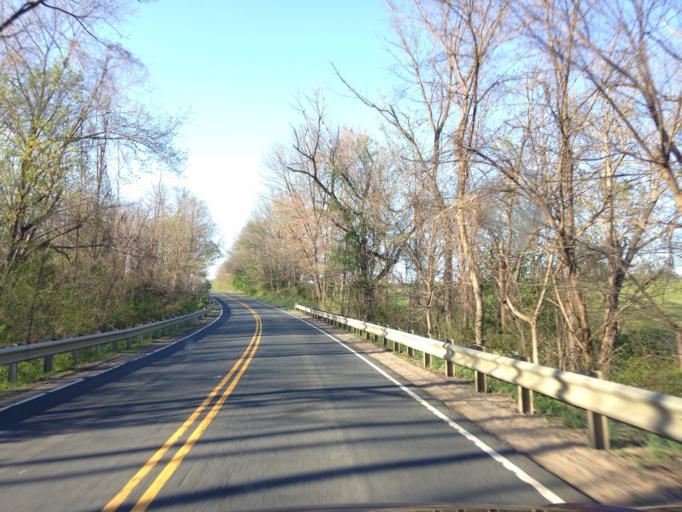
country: US
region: Virginia
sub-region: Loudoun County
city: Lovettsville
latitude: 39.2227
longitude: -77.6580
